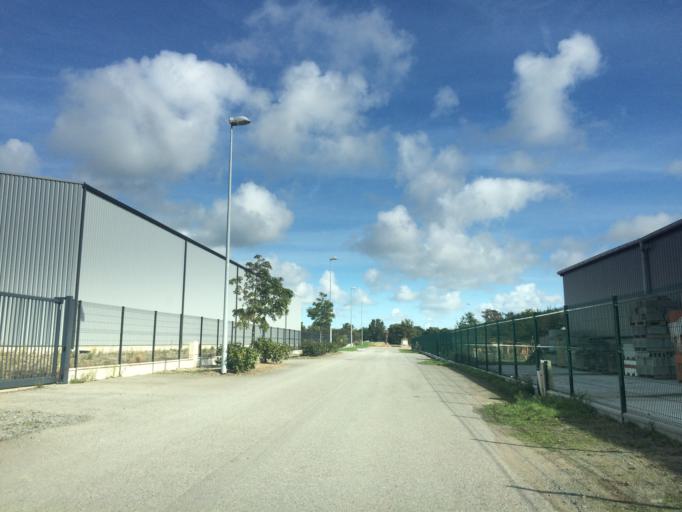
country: FR
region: Pays de la Loire
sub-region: Departement de la Loire-Atlantique
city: Chemere
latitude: 47.1283
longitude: -1.9067
